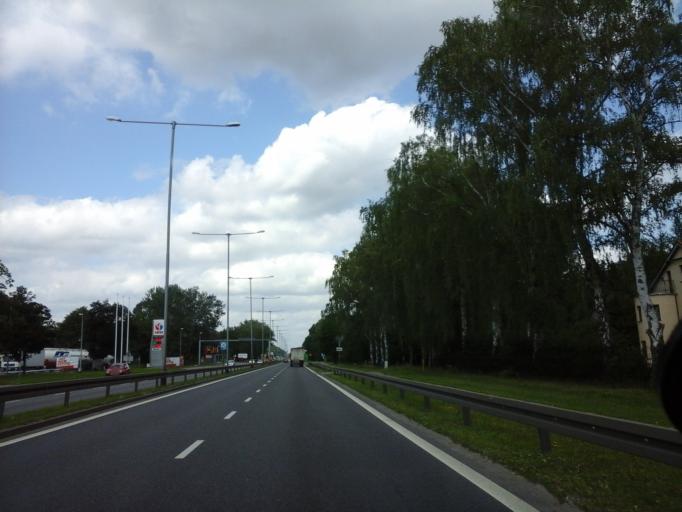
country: PL
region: West Pomeranian Voivodeship
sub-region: Powiat gryfinski
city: Stare Czarnowo
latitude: 53.3619
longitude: 14.7429
